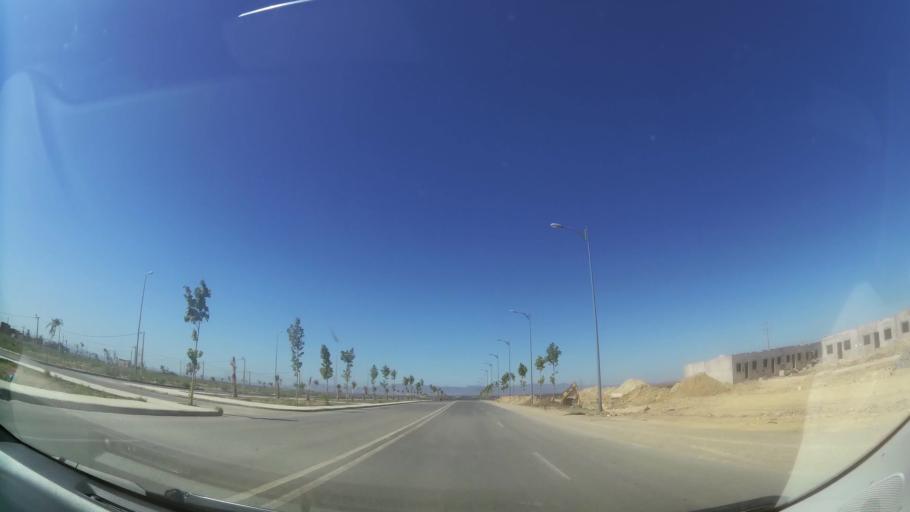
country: MA
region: Oriental
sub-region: Oujda-Angad
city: Oujda
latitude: 34.6823
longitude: -1.8585
